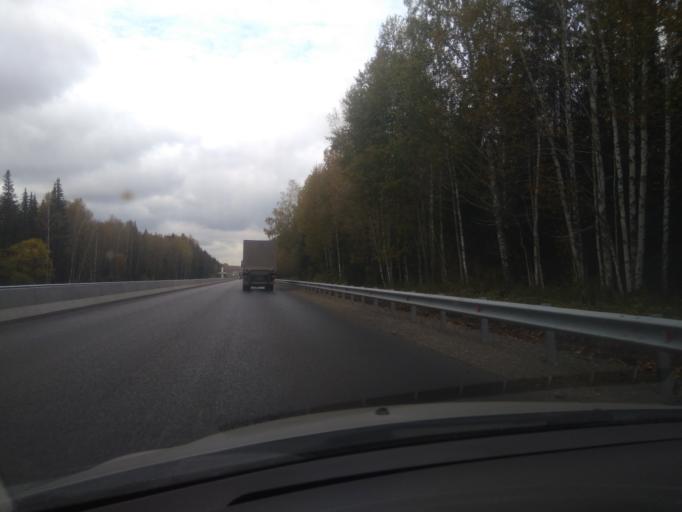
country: RU
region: Sverdlovsk
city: Yushala
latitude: 57.1031
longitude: 64.1900
